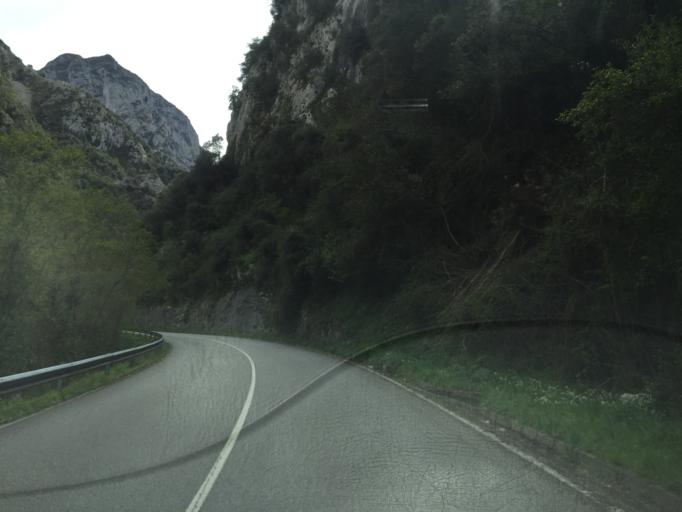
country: ES
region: Asturias
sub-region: Province of Asturias
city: Proaza
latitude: 43.2464
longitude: -6.0248
